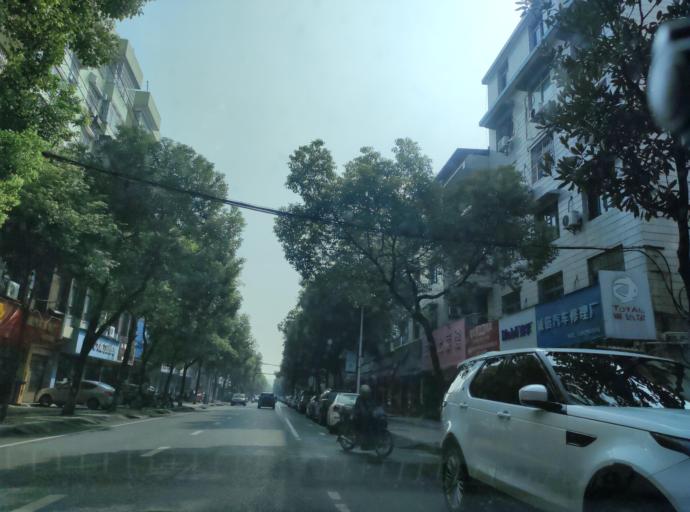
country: CN
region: Jiangxi Sheng
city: Pingxiang
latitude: 27.6433
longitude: 113.8571
